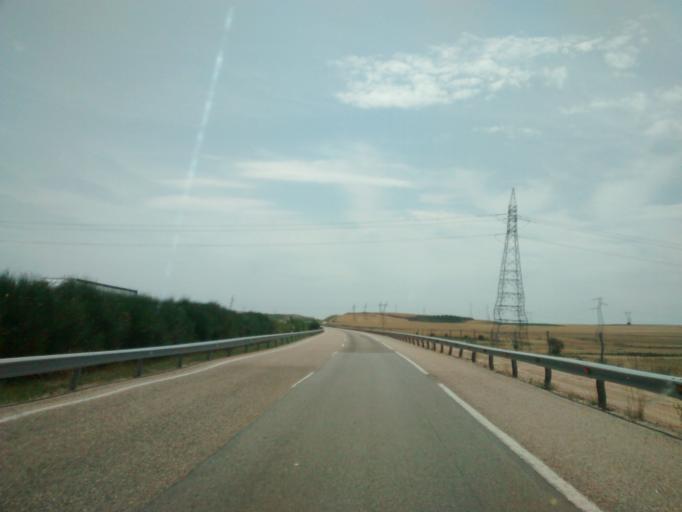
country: ES
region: Castille and Leon
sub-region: Provincia de Burgos
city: San Mames de Burgos
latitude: 42.3358
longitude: -3.7843
